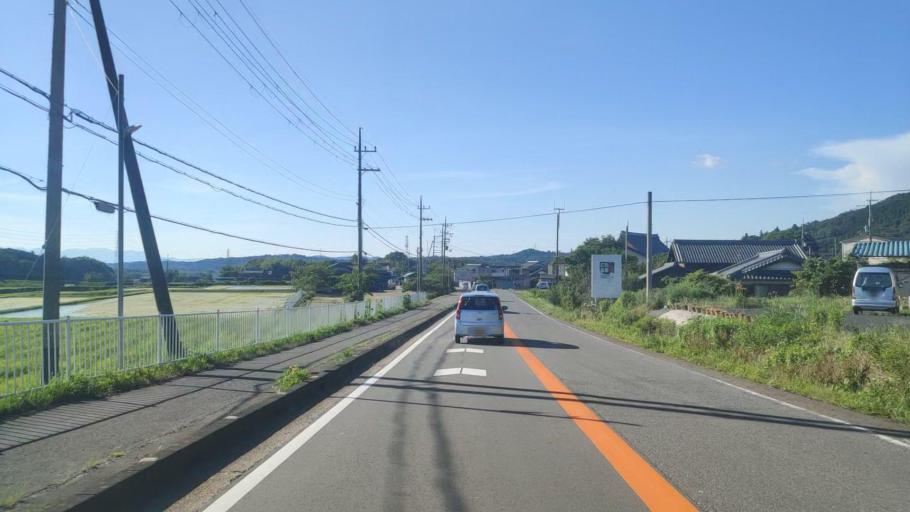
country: JP
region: Shiga Prefecture
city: Hino
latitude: 35.0439
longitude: 136.2407
